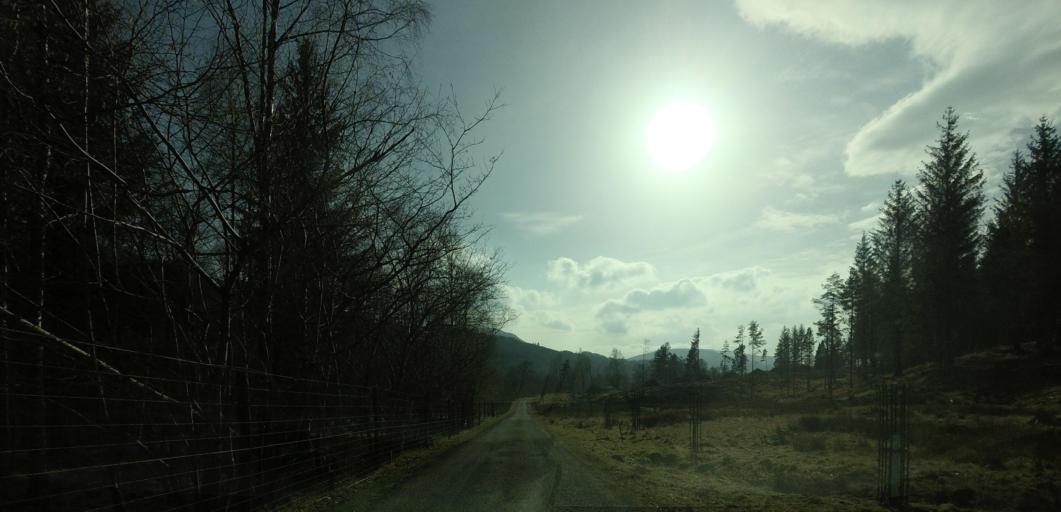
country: GB
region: Scotland
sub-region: Stirling
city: Callander
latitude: 56.5975
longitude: -4.3032
